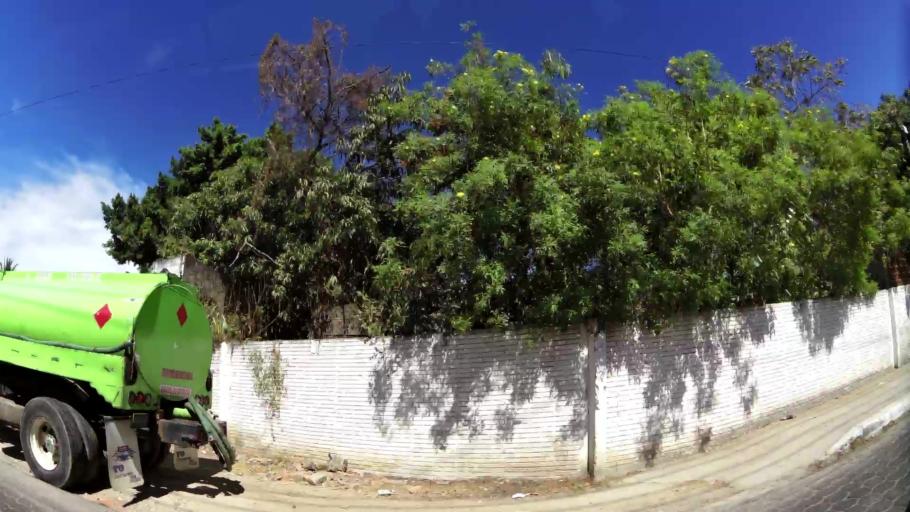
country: SV
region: San Salvador
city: Apopa
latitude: 13.8042
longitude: -89.1836
